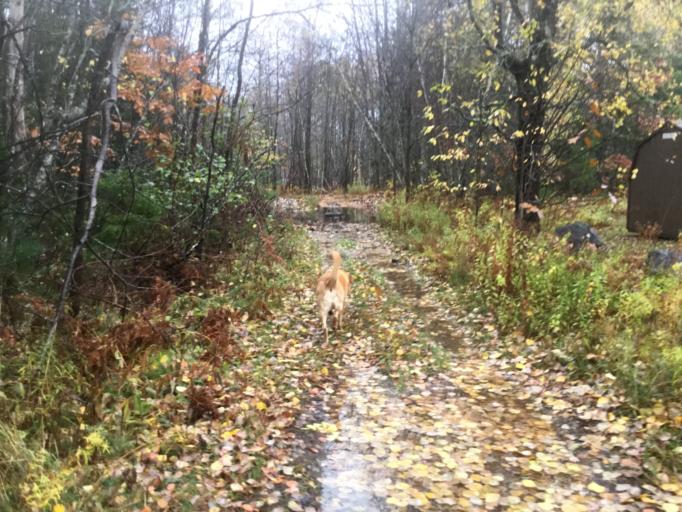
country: CA
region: Nova Scotia
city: New Glasgow
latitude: 45.5487
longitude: -62.6797
